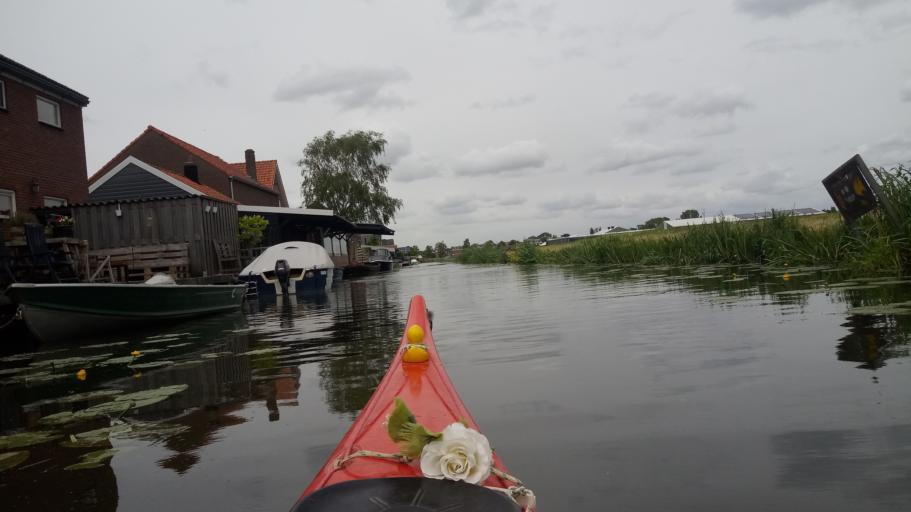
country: NL
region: North Holland
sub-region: Gemeente Enkhuizen
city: Enkhuizen
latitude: 52.6914
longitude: 5.2544
